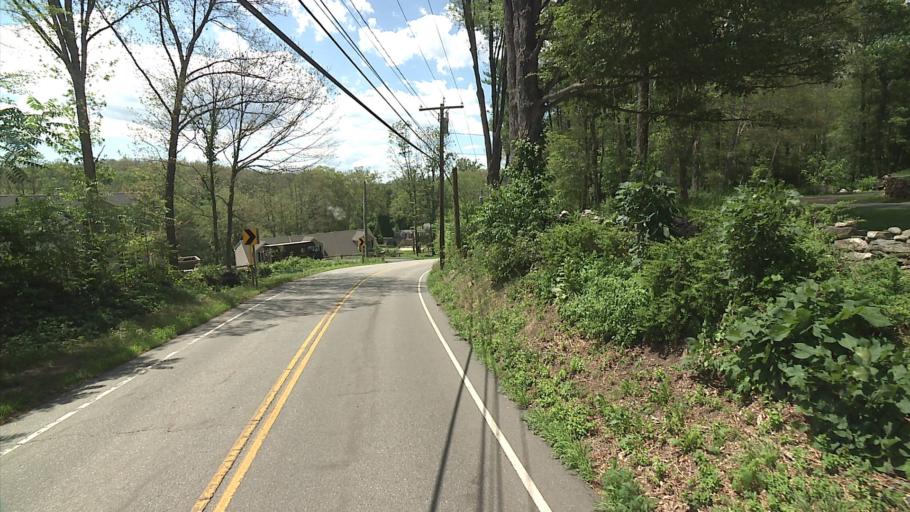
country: US
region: Connecticut
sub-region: Middlesex County
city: Moodus
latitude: 41.5011
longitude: -72.4677
